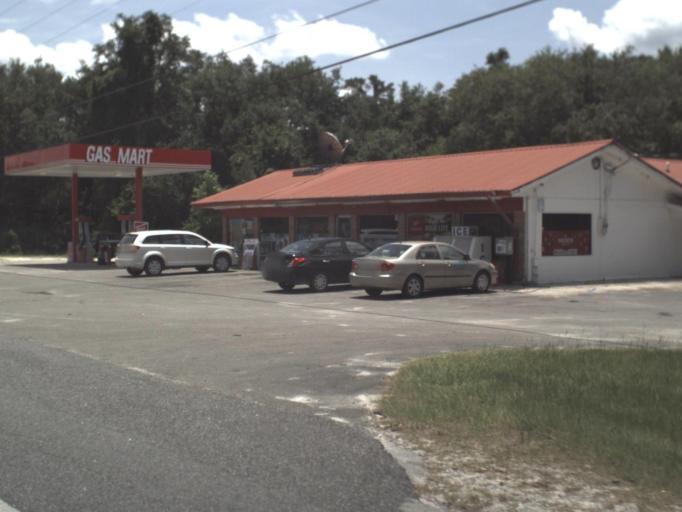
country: US
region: Florida
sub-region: Dixie County
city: Cross City
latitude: 29.6127
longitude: -83.0895
